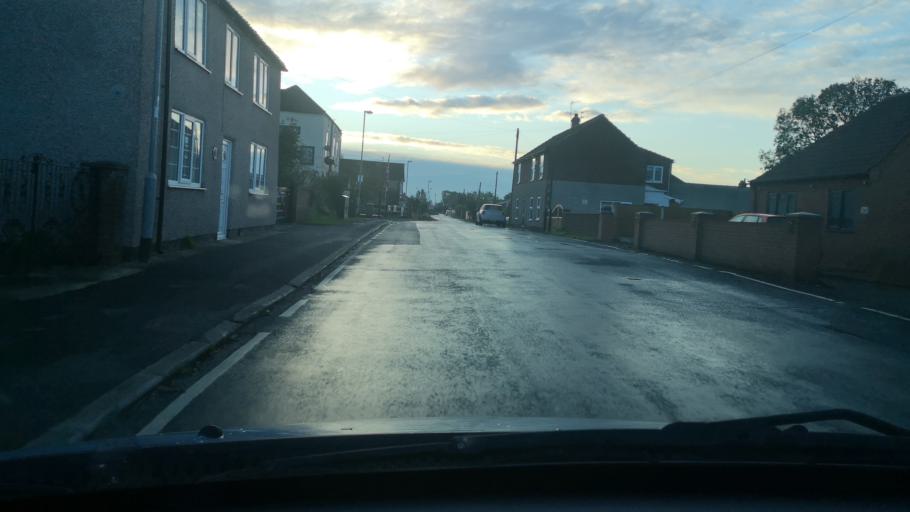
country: GB
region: England
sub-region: East Riding of Yorkshire
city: Laxton
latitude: 53.6985
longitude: -0.7951
